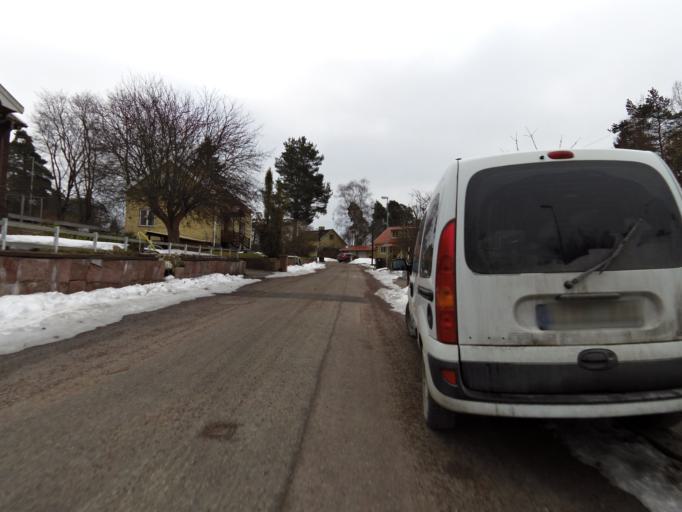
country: SE
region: Gaevleborg
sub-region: Gavle Kommun
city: Gavle
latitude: 60.6618
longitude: 17.1251
